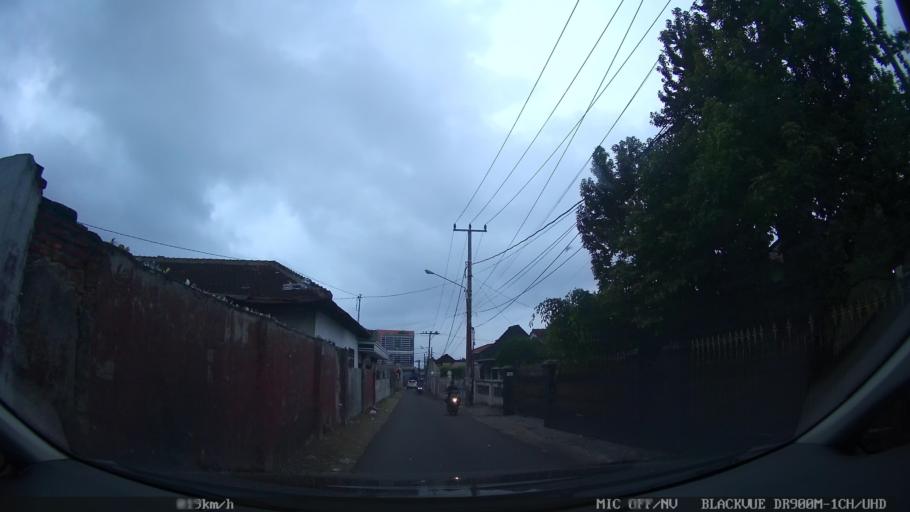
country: ID
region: Lampung
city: Bandarlampung
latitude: -5.4108
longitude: 105.2790
